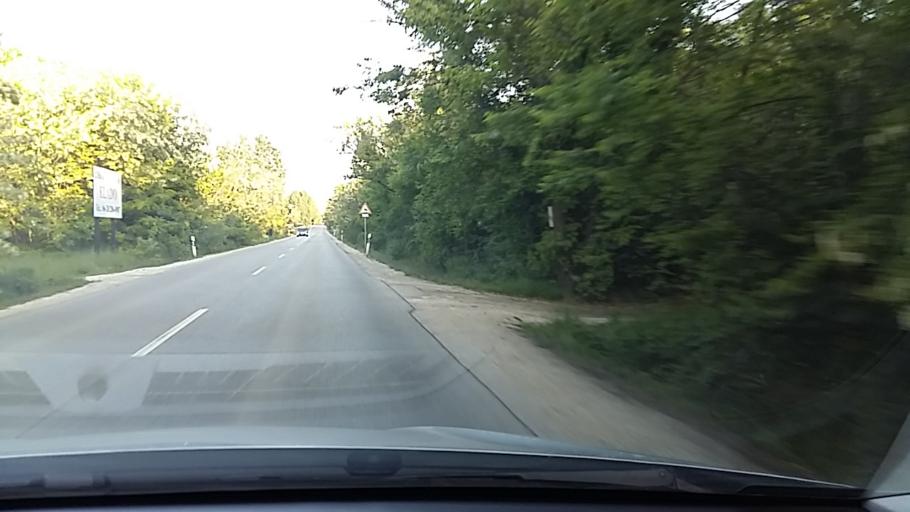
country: HU
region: Pest
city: Orbottyan
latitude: 47.6956
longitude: 19.2486
